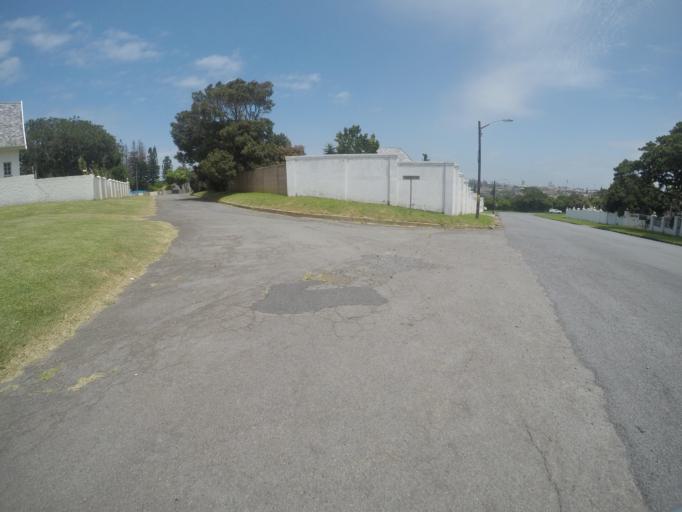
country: ZA
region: Eastern Cape
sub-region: Buffalo City Metropolitan Municipality
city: East London
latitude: -33.0005
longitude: 27.9277
